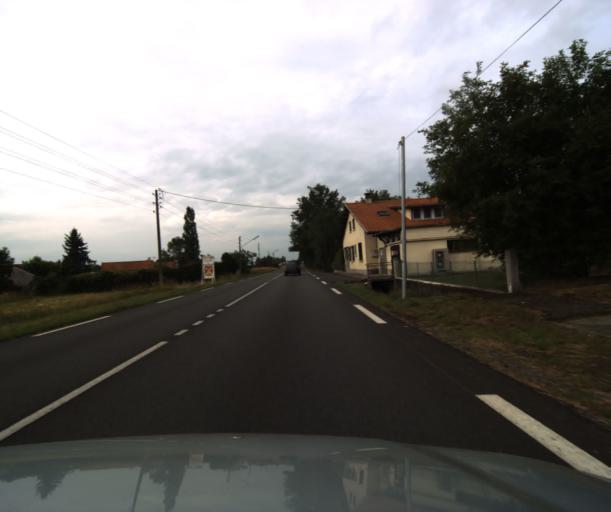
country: FR
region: Midi-Pyrenees
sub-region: Departement des Hautes-Pyrenees
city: Rabastens-de-Bigorre
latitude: 43.3809
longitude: 0.1483
